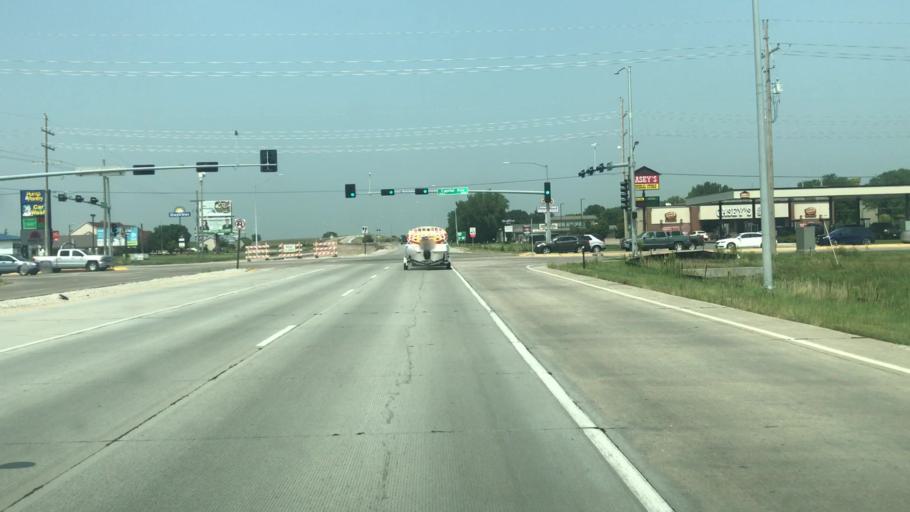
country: US
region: Nebraska
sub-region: Hall County
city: Grand Island
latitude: 40.9454
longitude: -98.3835
